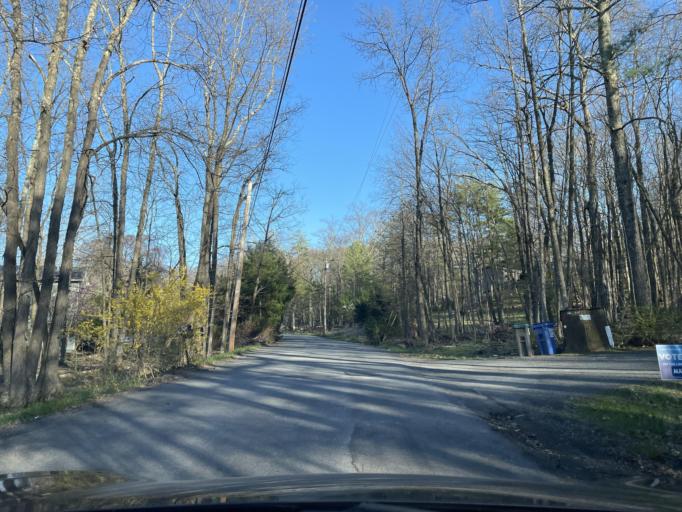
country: US
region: New York
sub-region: Ulster County
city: Woodstock
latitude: 42.0297
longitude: -74.1136
